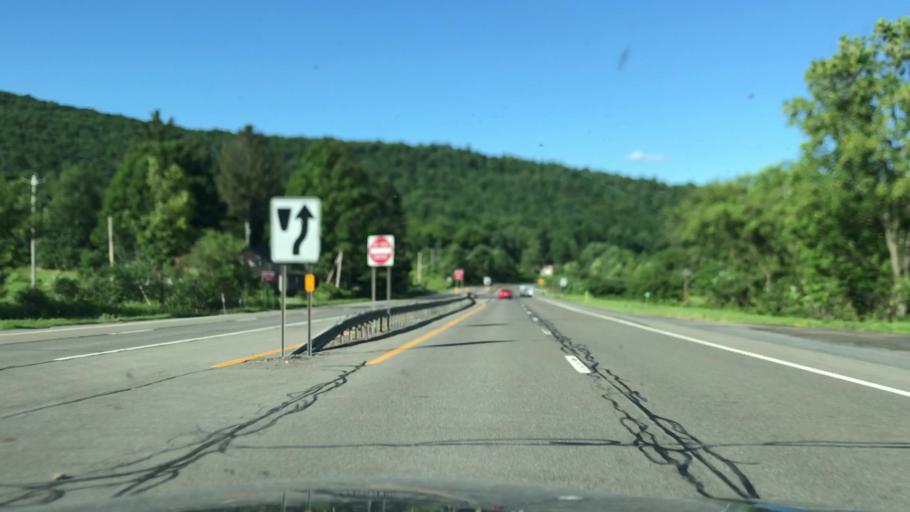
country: US
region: New York
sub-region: Broome County
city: Deposit
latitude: 42.0070
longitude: -75.3723
